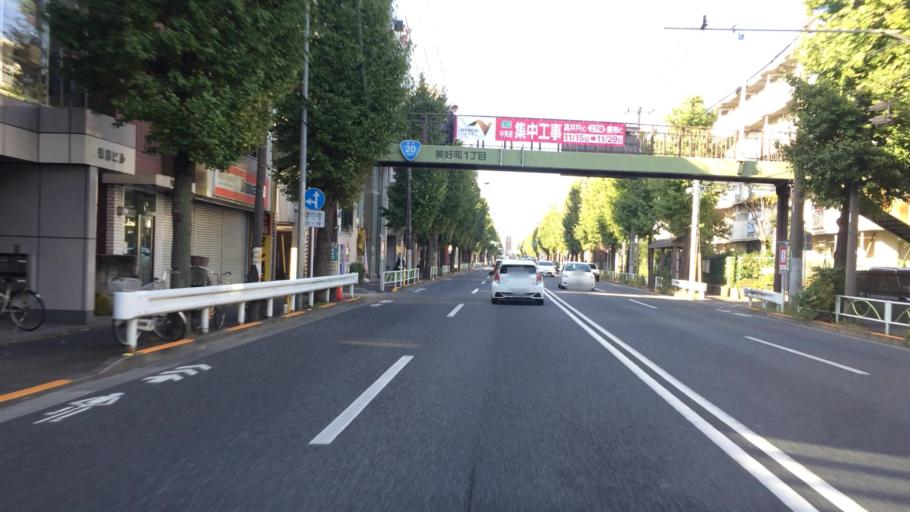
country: JP
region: Tokyo
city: Kokubunji
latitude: 35.6730
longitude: 139.4695
